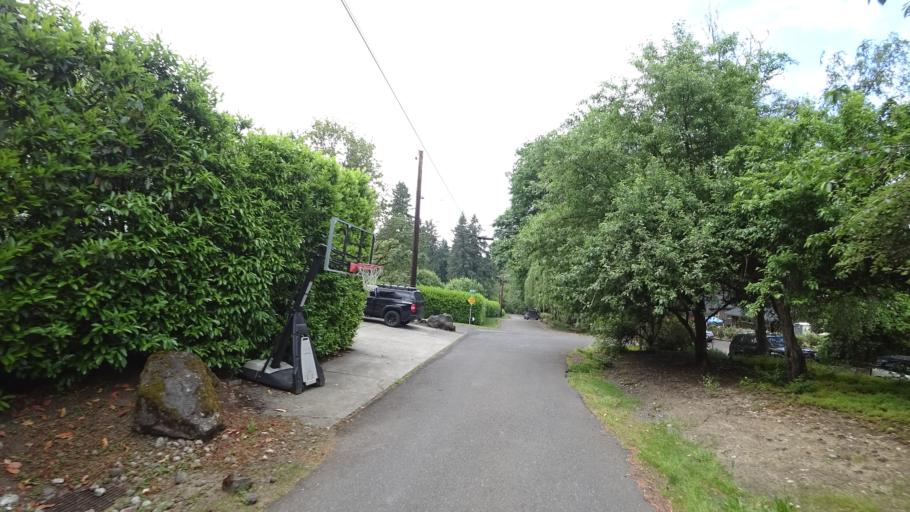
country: US
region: Oregon
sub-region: Clackamas County
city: Milwaukie
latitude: 45.4491
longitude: -122.6629
